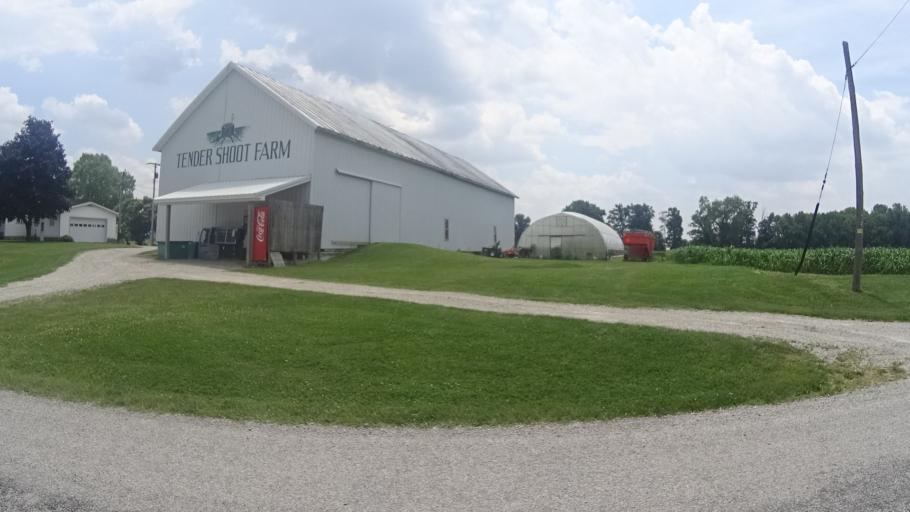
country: US
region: Ohio
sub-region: Erie County
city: Milan
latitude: 41.3076
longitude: -82.6347
